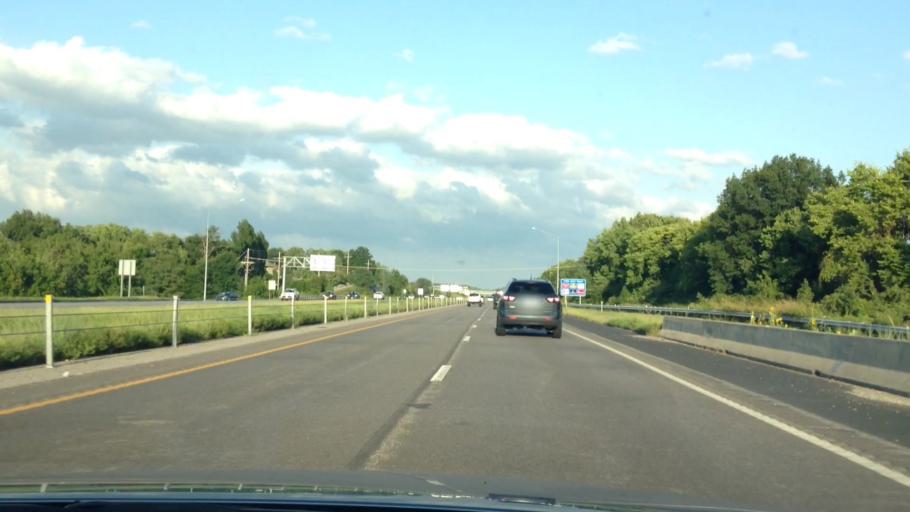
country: US
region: Missouri
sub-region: Platte County
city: Weatherby Lake
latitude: 39.2539
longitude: -94.6472
